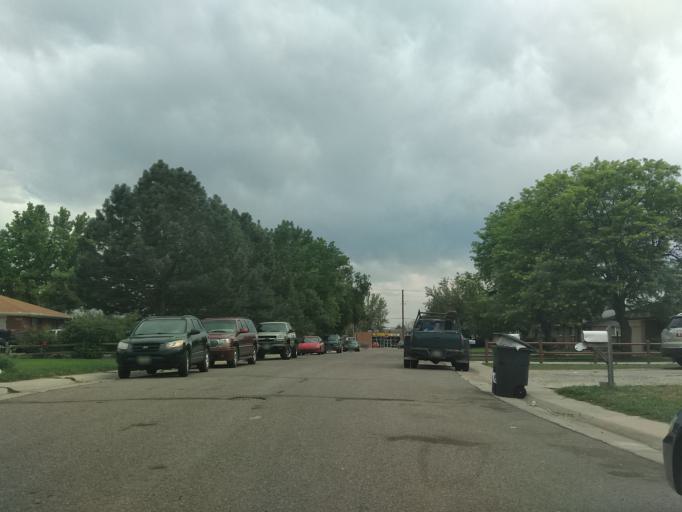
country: US
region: Colorado
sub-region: Jefferson County
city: Lakewood
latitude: 39.6981
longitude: -105.0839
